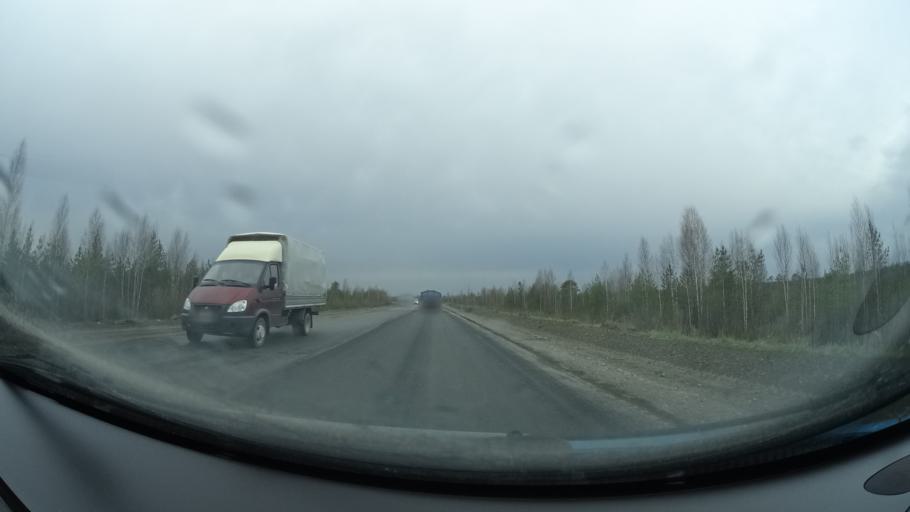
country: RU
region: Perm
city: Krasnokamsk
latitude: 58.0884
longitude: 55.6900
